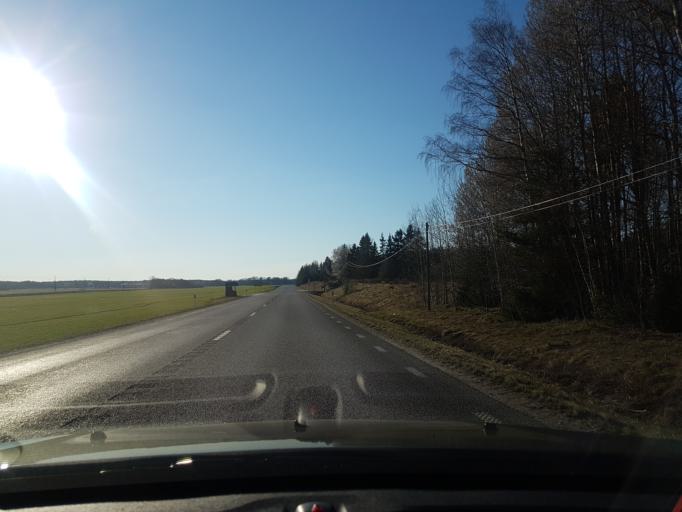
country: SE
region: Uppsala
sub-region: Enkopings Kommun
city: Orsundsbro
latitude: 59.8693
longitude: 17.3165
